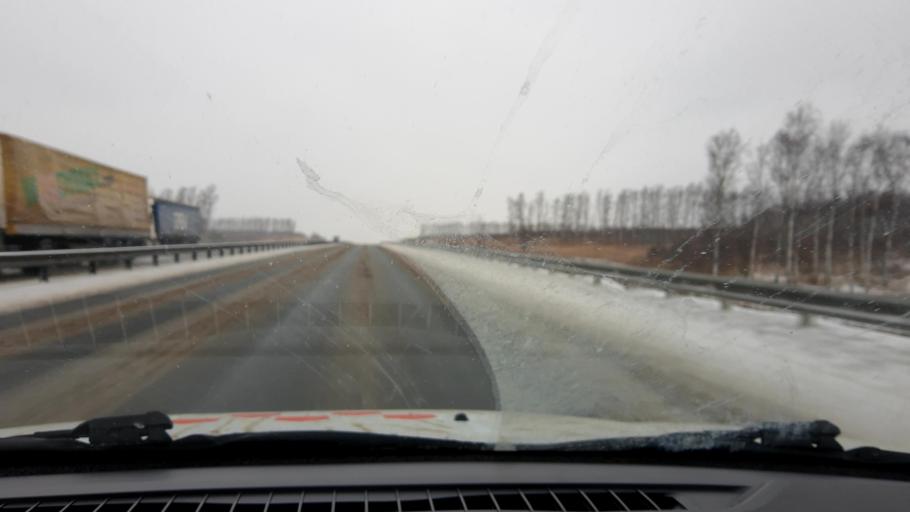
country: RU
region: Nizjnij Novgorod
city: Afonino
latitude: 56.1023
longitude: 44.0165
